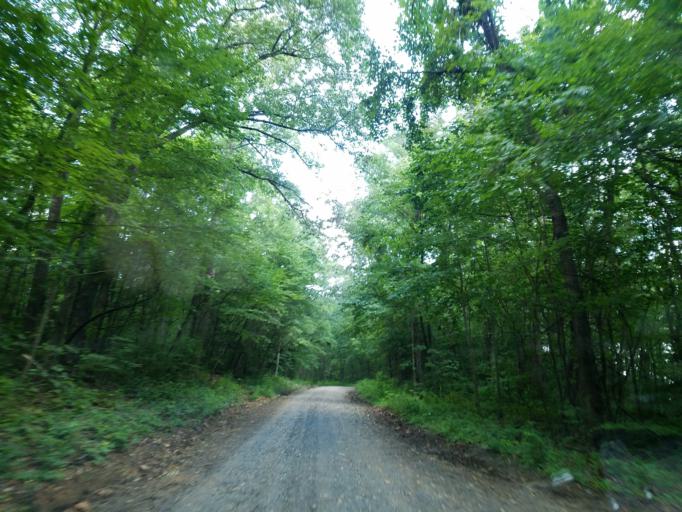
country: US
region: Georgia
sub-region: Dawson County
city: Dawsonville
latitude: 34.6444
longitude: -84.2062
